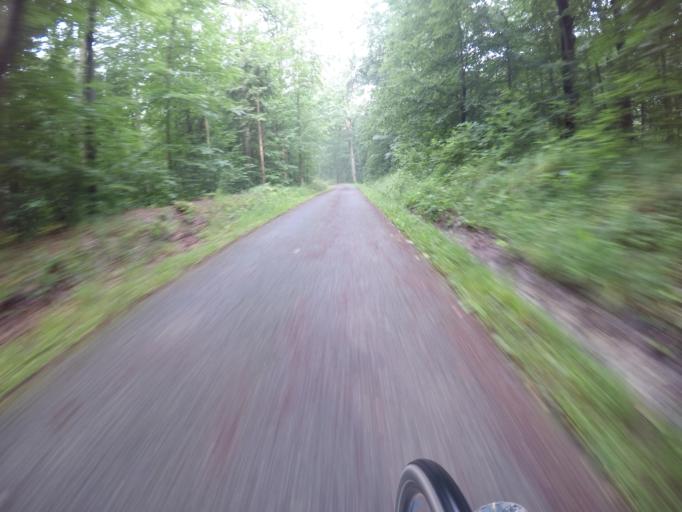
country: DE
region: Baden-Wuerttemberg
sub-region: Regierungsbezirk Stuttgart
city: Sindelfingen
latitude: 48.7122
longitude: 9.0482
